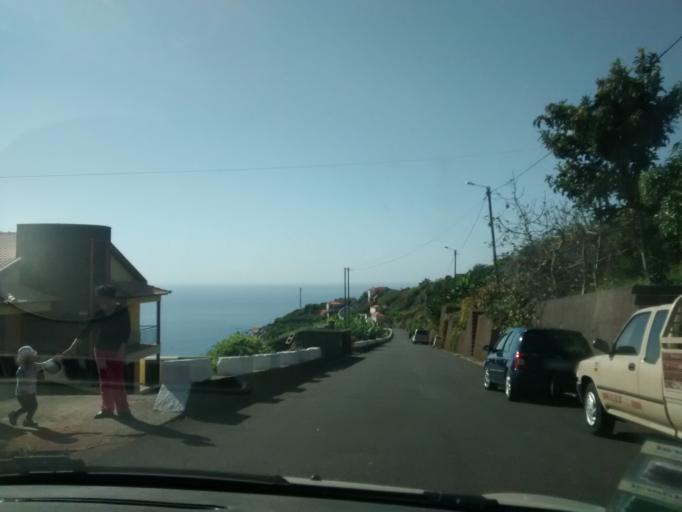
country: PT
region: Madeira
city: Calheta
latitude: 32.7237
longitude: -17.1684
